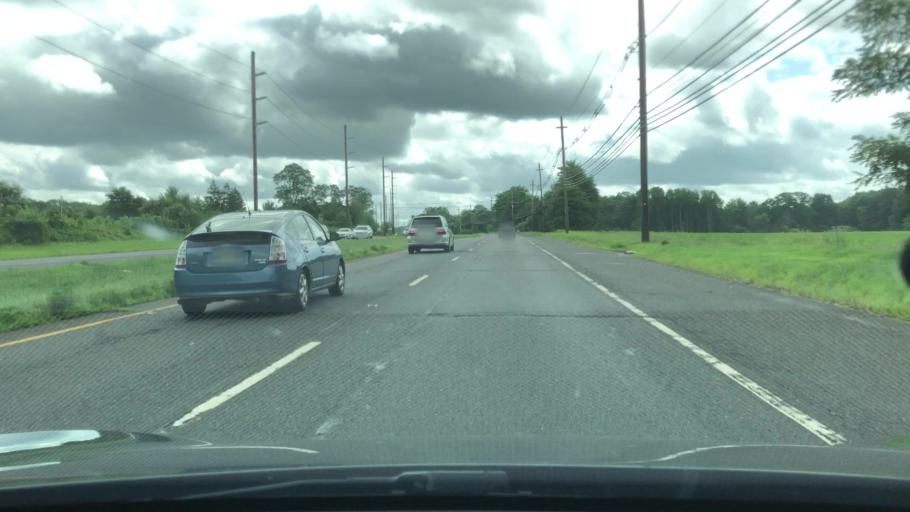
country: US
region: New Jersey
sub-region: Mercer County
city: Twin Rivers
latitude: 40.2645
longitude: -74.4530
